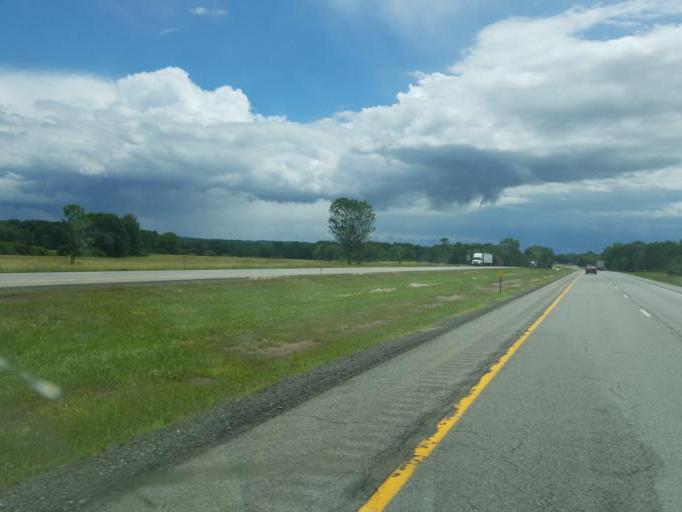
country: US
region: New York
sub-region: Monroe County
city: Pittsford
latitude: 43.0205
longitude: -77.4940
